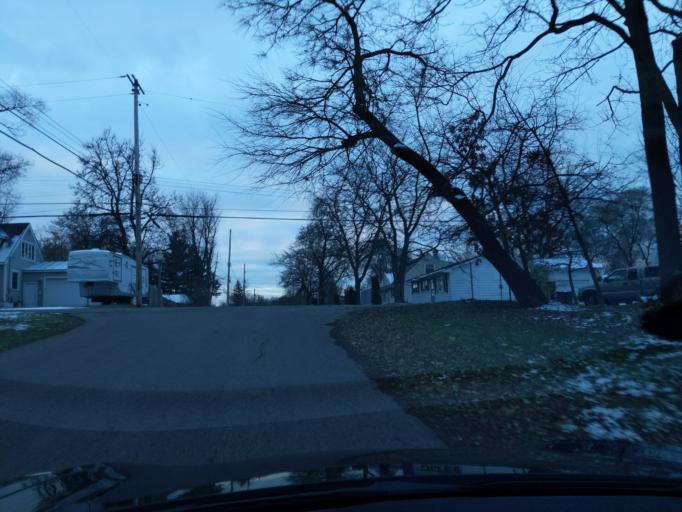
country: US
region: Michigan
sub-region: Ingham County
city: Lansing
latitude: 42.7681
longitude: -84.5496
